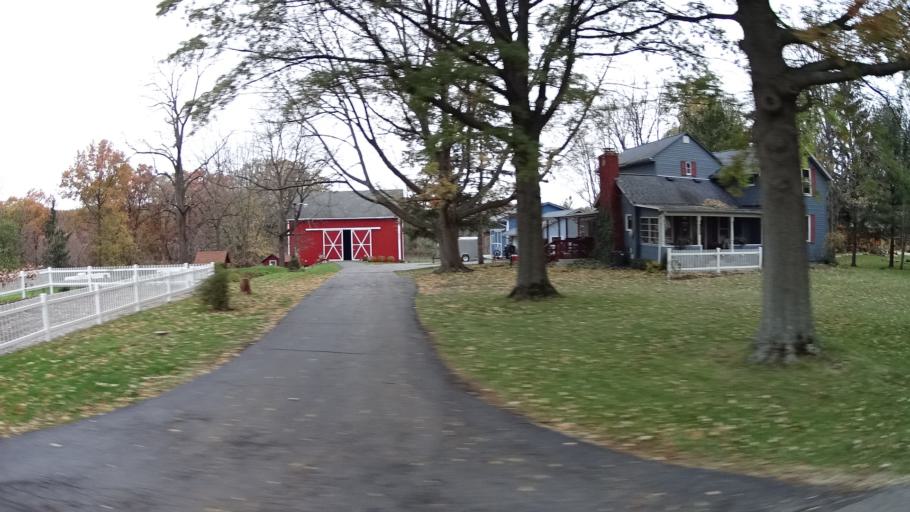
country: US
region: Ohio
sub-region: Lorain County
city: Sheffield
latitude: 41.4140
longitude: -82.0998
